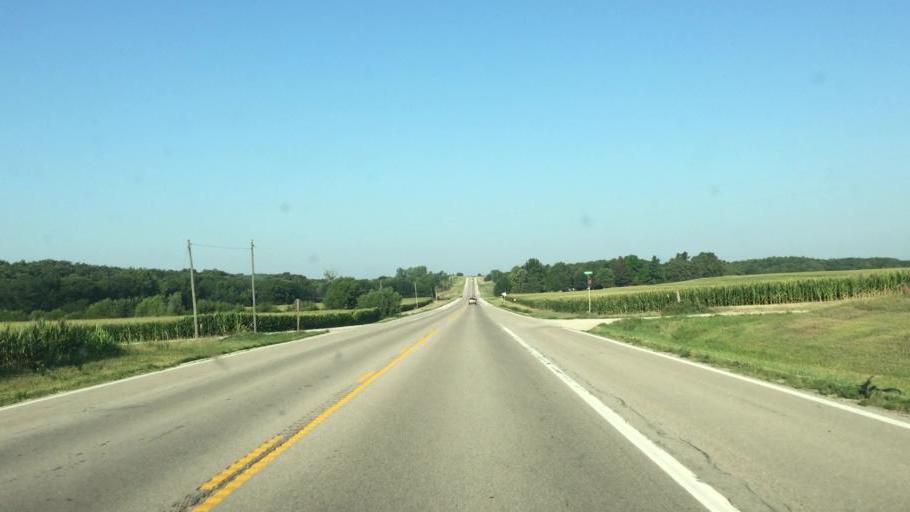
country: US
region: Kansas
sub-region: Nemaha County
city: Sabetha
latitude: 39.8466
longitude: -95.6760
